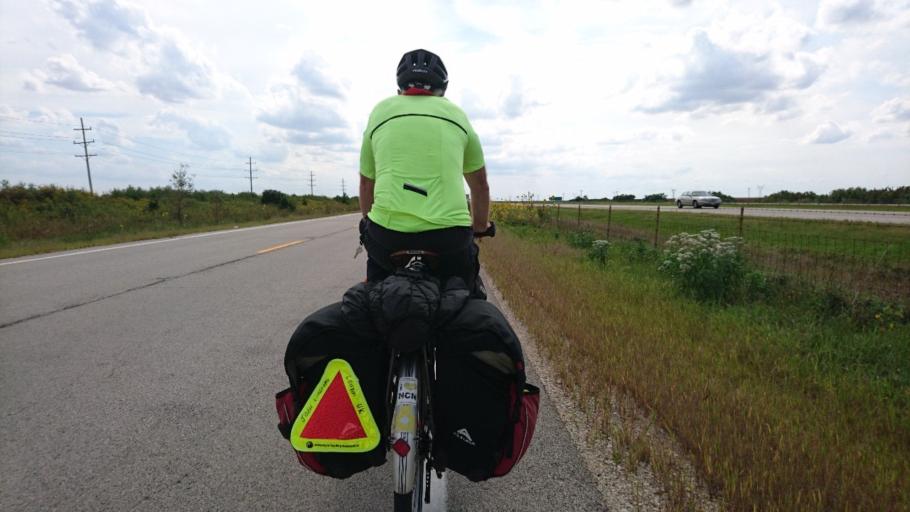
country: US
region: Illinois
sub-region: Grundy County
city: Gardner
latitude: 41.1669
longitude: -88.3351
